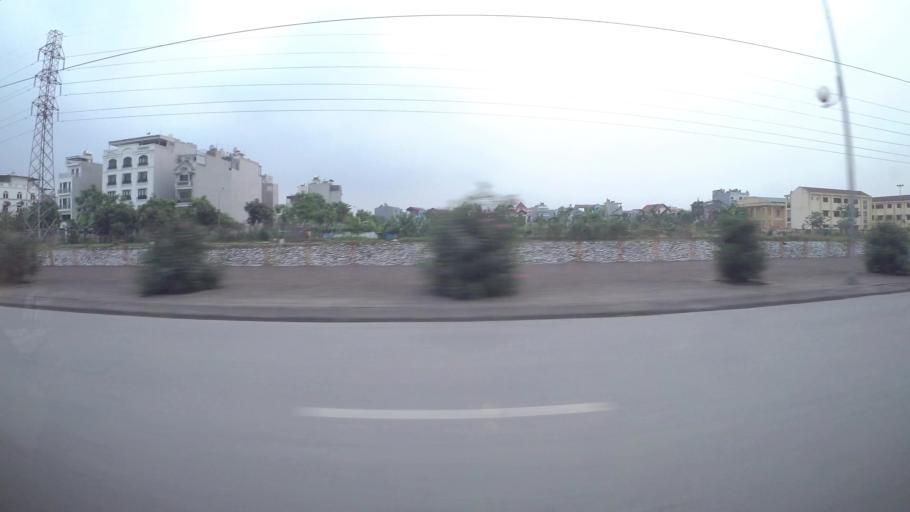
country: VN
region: Ha Noi
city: Trau Quy
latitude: 21.0597
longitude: 105.9029
